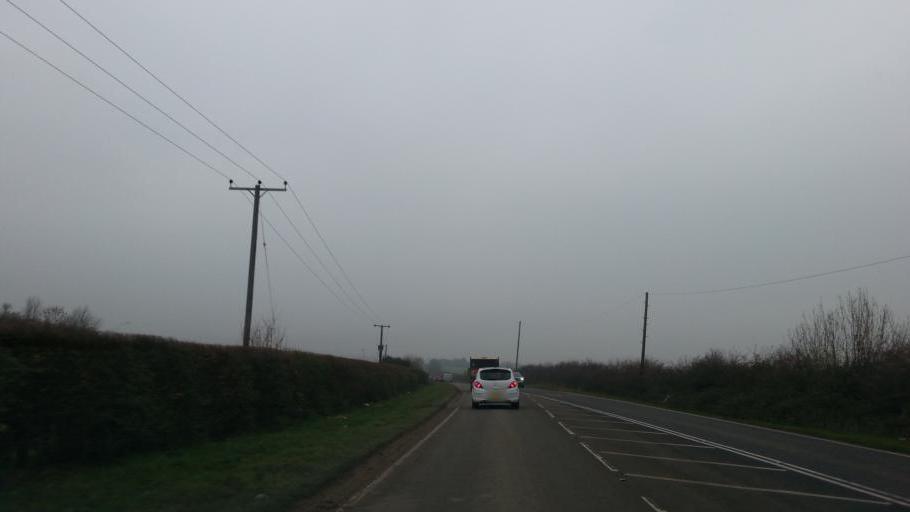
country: GB
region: England
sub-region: Cambridgeshire
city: Godmanchester
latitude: 52.2990
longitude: -0.1546
